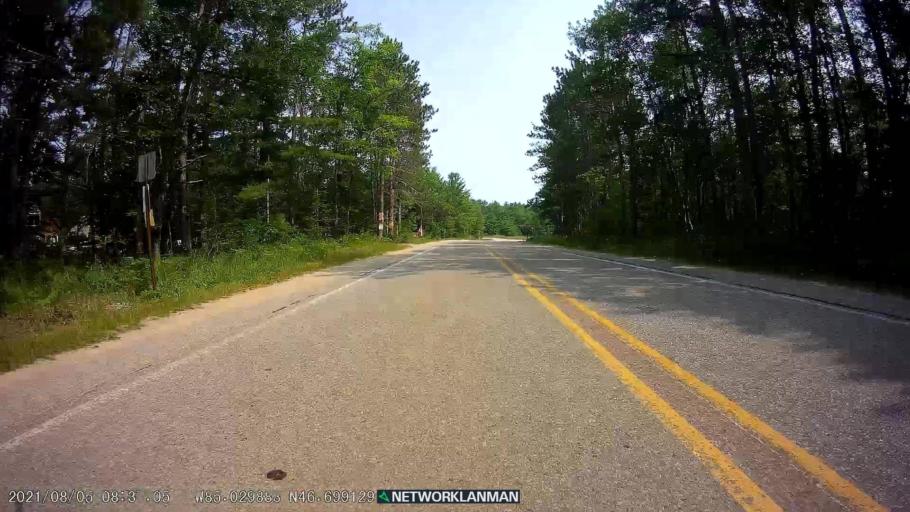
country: US
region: Michigan
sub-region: Luce County
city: Newberry
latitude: 46.6989
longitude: -85.0300
